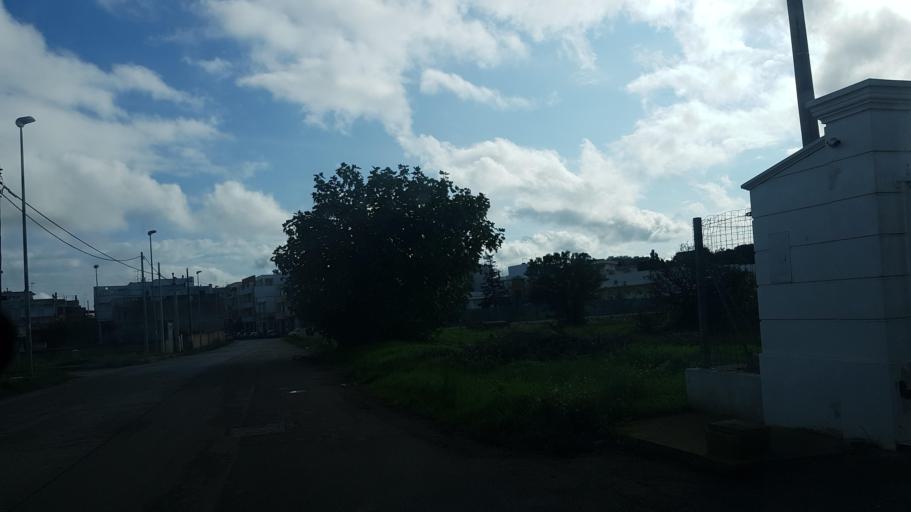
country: IT
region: Apulia
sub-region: Provincia di Brindisi
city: Carovigno
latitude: 40.7151
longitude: 17.6558
